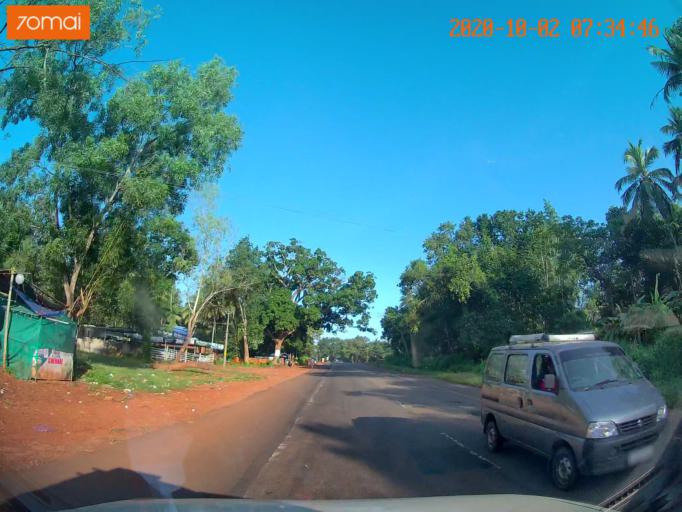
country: IN
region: Kerala
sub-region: Malappuram
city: Pariyapuram
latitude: 11.0652
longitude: 75.9264
